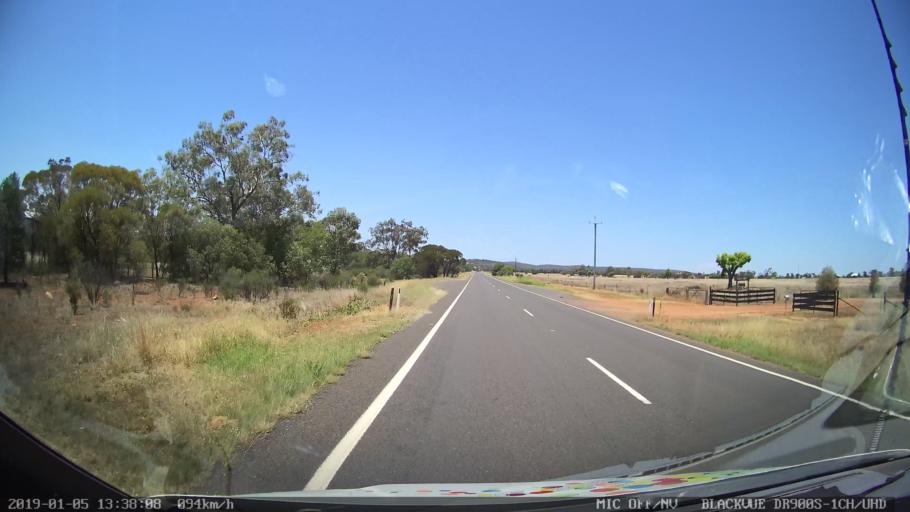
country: AU
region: New South Wales
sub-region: Gunnedah
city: Gunnedah
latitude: -30.9834
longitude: 150.1933
